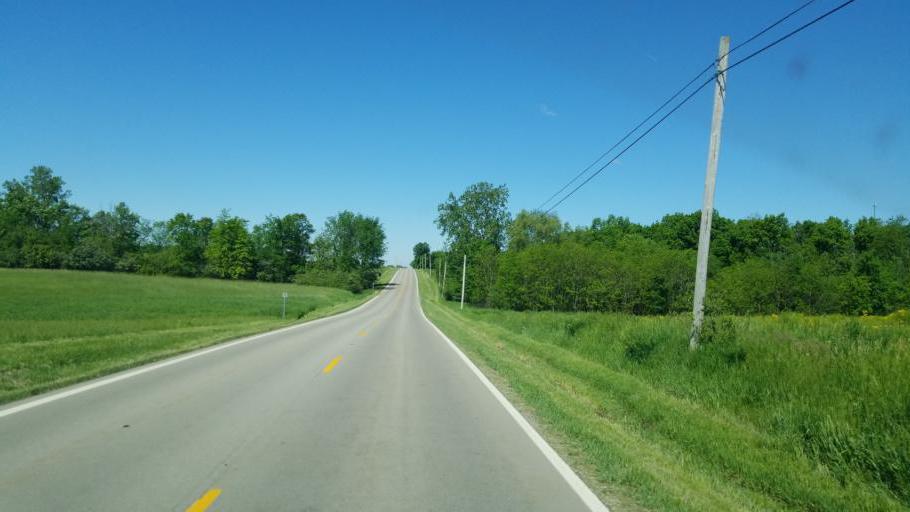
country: US
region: Ohio
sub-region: Logan County
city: Northwood
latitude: 40.4593
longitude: -83.6822
